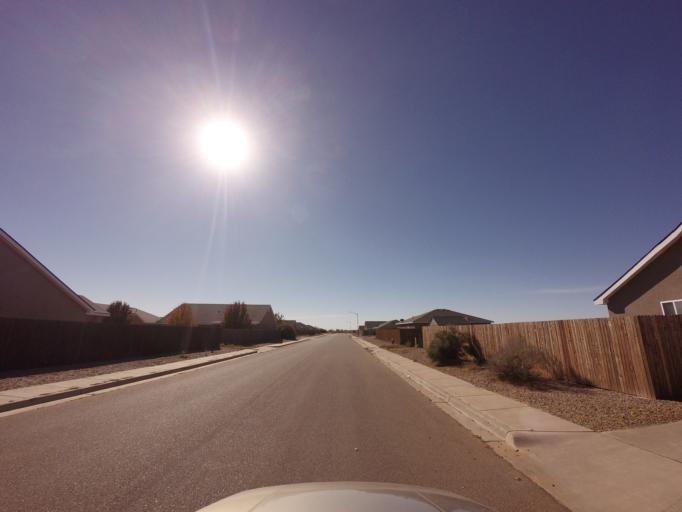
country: US
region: New Mexico
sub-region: Curry County
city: Clovis
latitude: 34.4145
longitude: -103.1624
